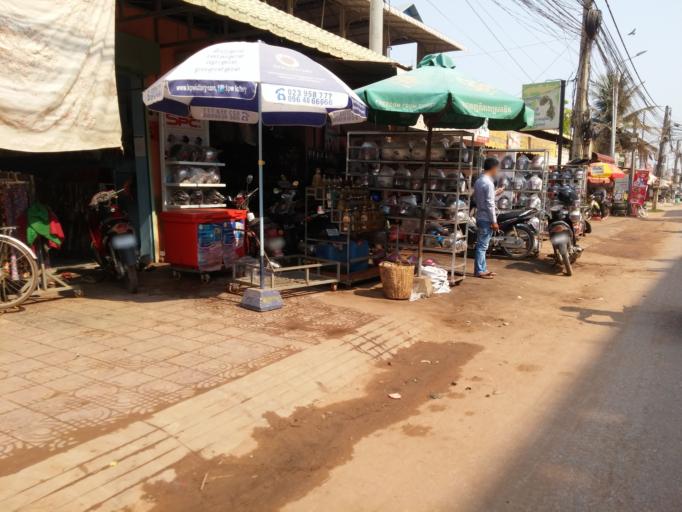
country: KH
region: Siem Reap
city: Siem Reap
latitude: 13.3786
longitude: 103.8516
